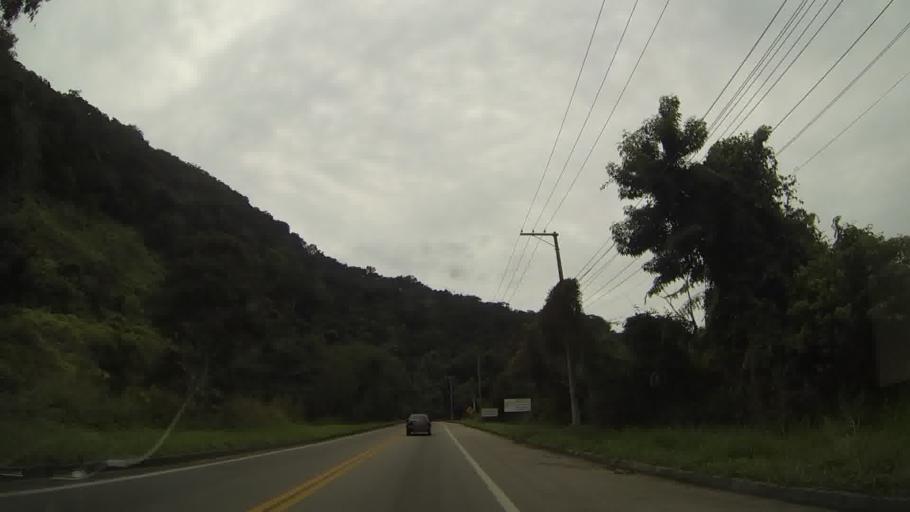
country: BR
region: Sao Paulo
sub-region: Sao Sebastiao
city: Sao Sebastiao
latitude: -23.8231
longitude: -45.4451
